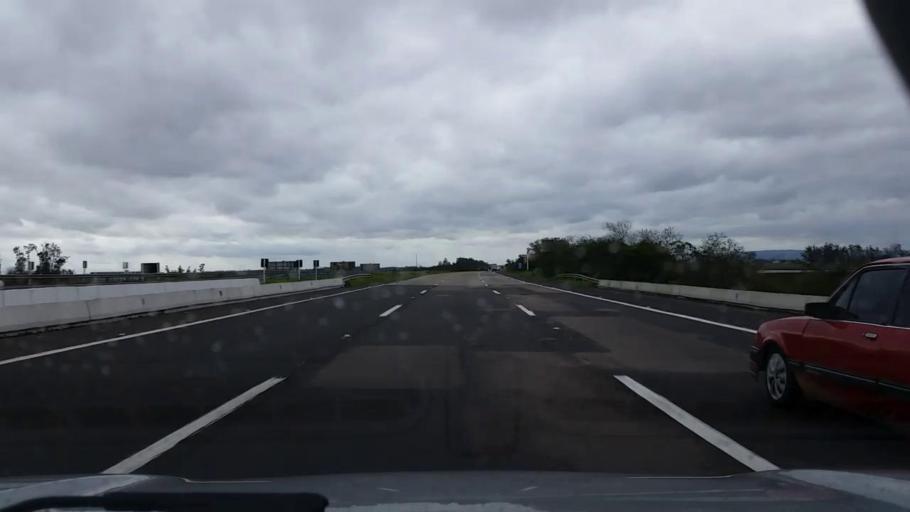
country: BR
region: Rio Grande do Sul
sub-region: Rolante
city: Rolante
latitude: -29.8863
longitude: -50.6360
